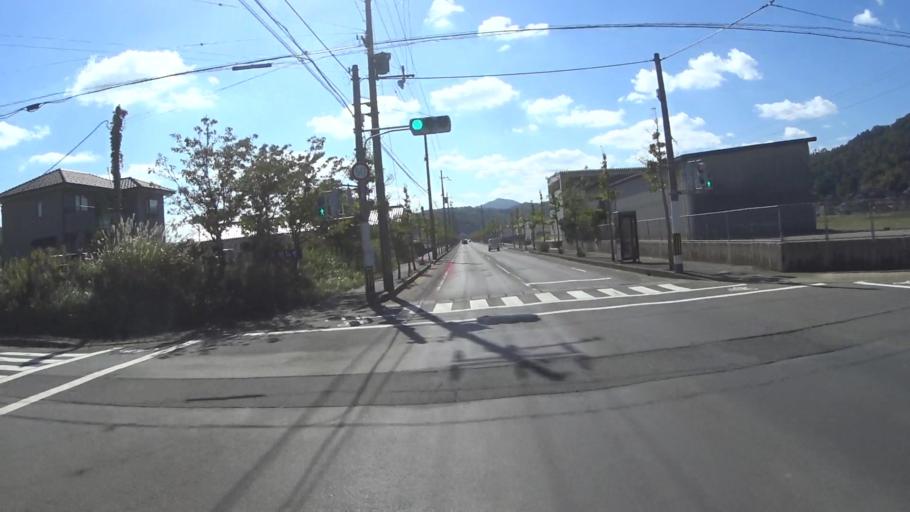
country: JP
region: Kyoto
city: Miyazu
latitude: 35.6751
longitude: 135.0249
